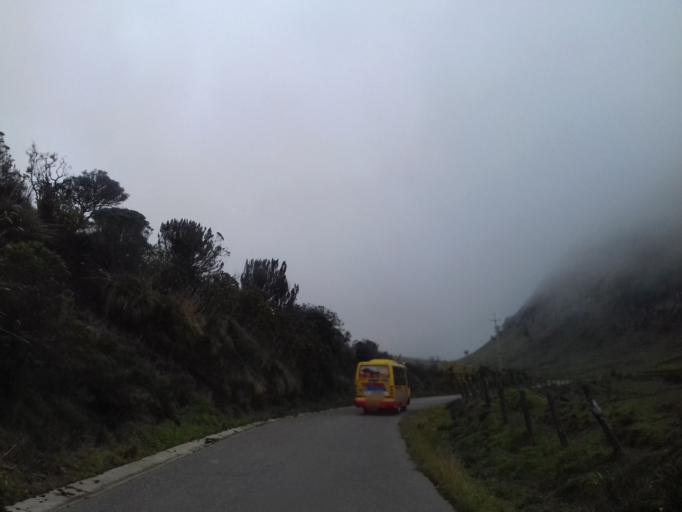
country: CO
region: Caldas
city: Villamaria
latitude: 4.9857
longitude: -75.3337
